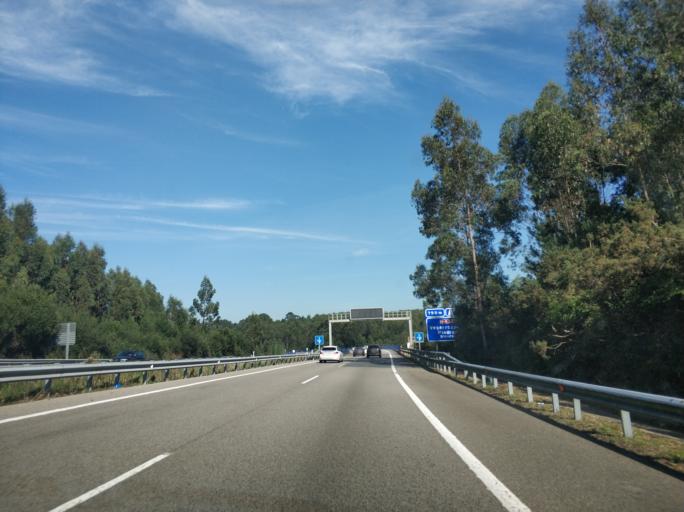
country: ES
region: Asturias
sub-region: Province of Asturias
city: Castrillon
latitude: 43.5453
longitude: -6.0128
